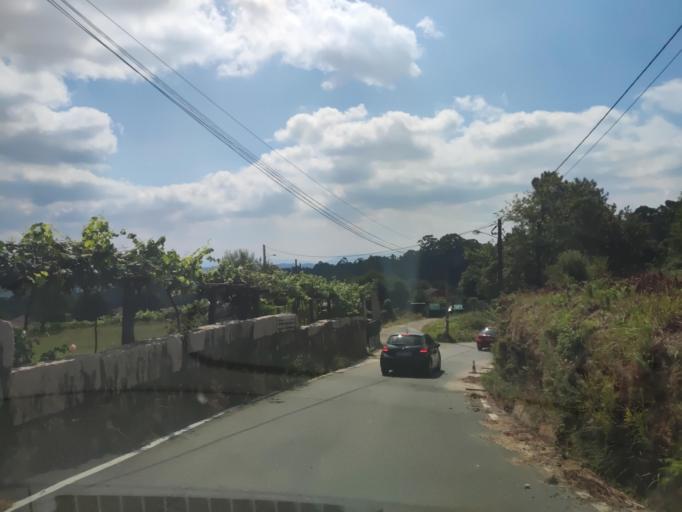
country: ES
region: Galicia
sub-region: Provincia de Pontevedra
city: Porrino
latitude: 42.1523
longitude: -8.6500
